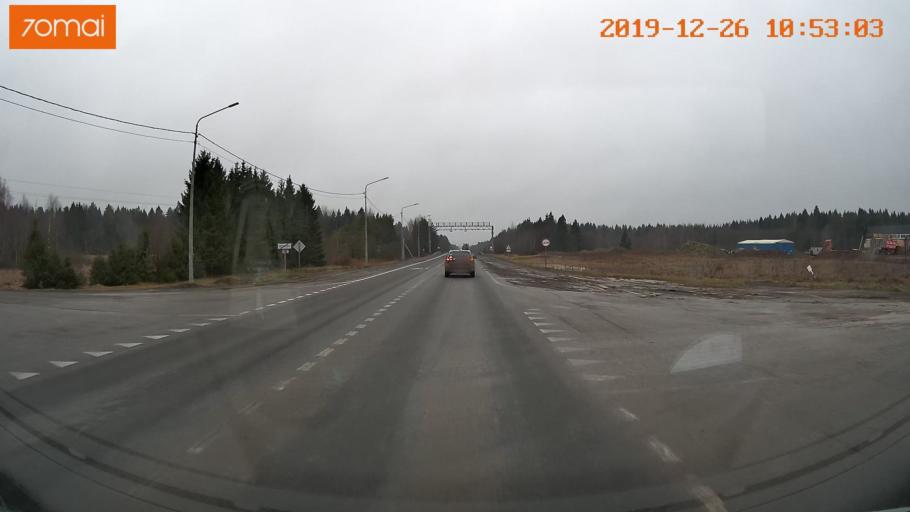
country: RU
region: Vologda
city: Molochnoye
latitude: 59.1974
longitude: 39.6314
